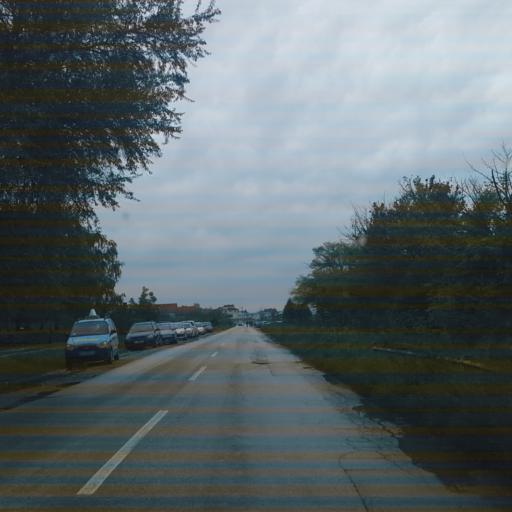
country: RS
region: Central Serbia
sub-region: Nisavski Okrug
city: Aleksinac
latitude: 43.5554
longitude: 21.6881
